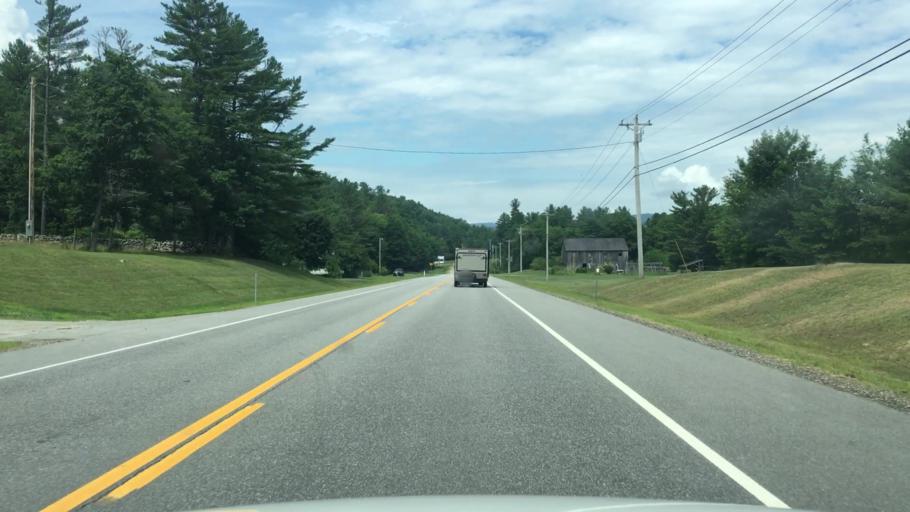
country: US
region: New Hampshire
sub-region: Grafton County
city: Rumney
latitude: 43.8310
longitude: -71.8968
